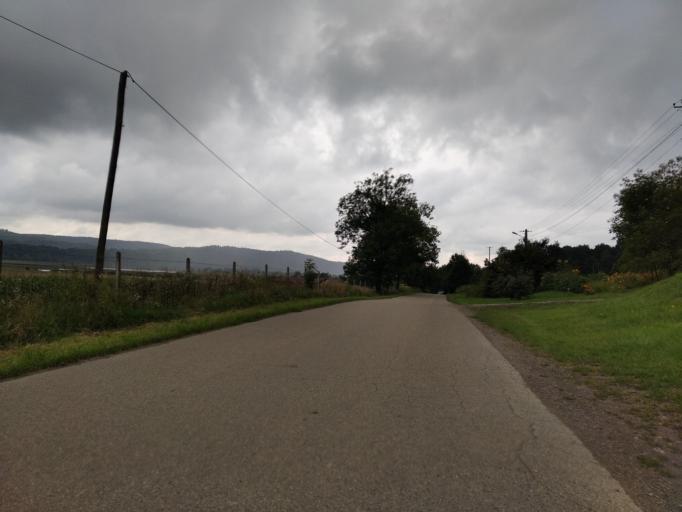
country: PL
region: Subcarpathian Voivodeship
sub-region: Powiat brzozowski
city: Dydnia
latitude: 49.6744
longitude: 22.2762
